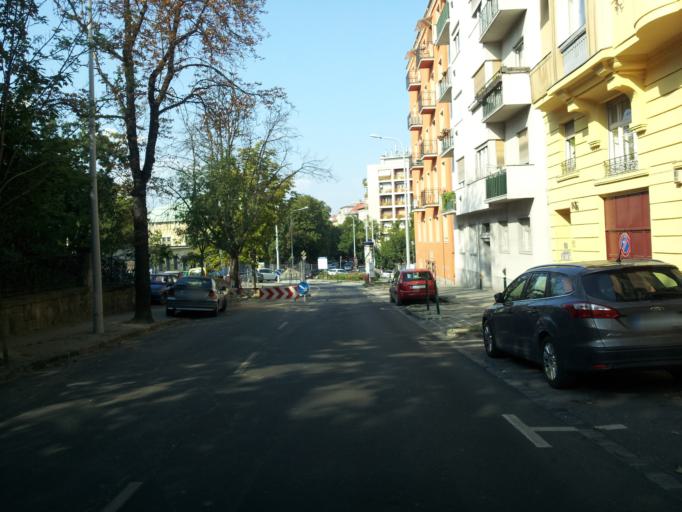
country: HU
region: Budapest
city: Budapest XII. keruelet
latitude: 47.4968
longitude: 19.0194
